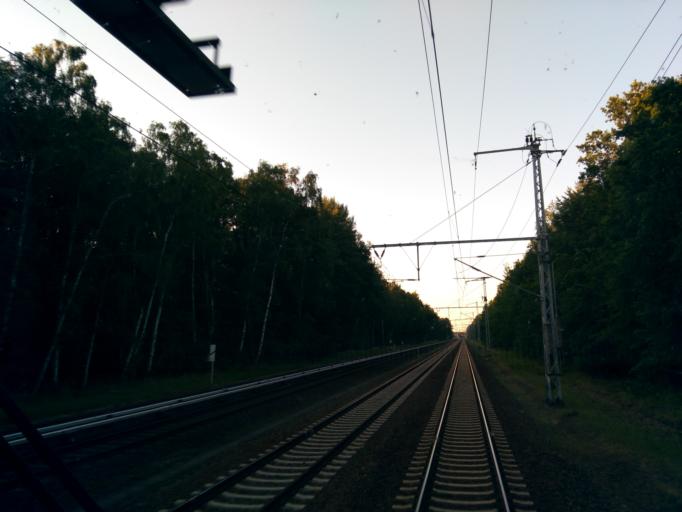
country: DE
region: Brandenburg
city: Zeuthen
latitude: 52.3848
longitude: 13.6064
